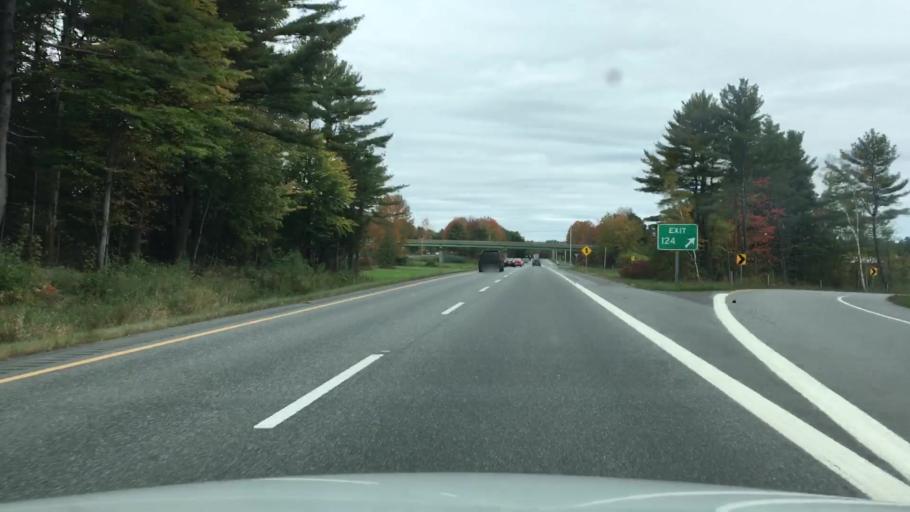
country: US
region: Maine
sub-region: Kennebec County
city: Oakland
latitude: 44.5056
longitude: -69.7032
